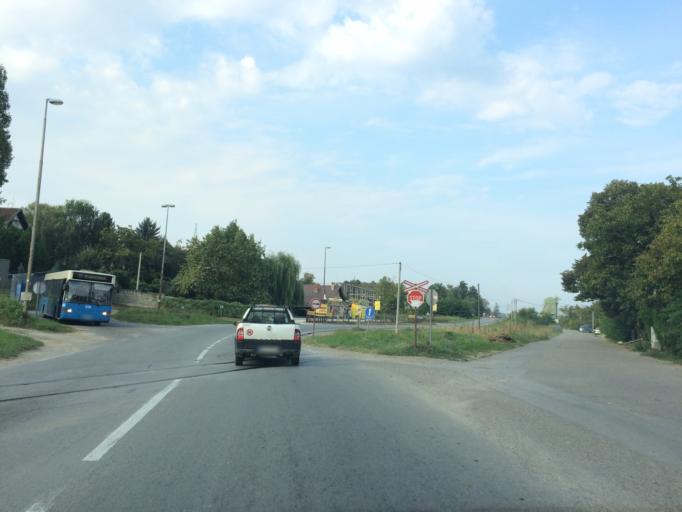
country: RS
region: Autonomna Pokrajina Vojvodina
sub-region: Juznobacki Okrug
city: Novi Sad
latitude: 45.2183
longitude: 19.8186
